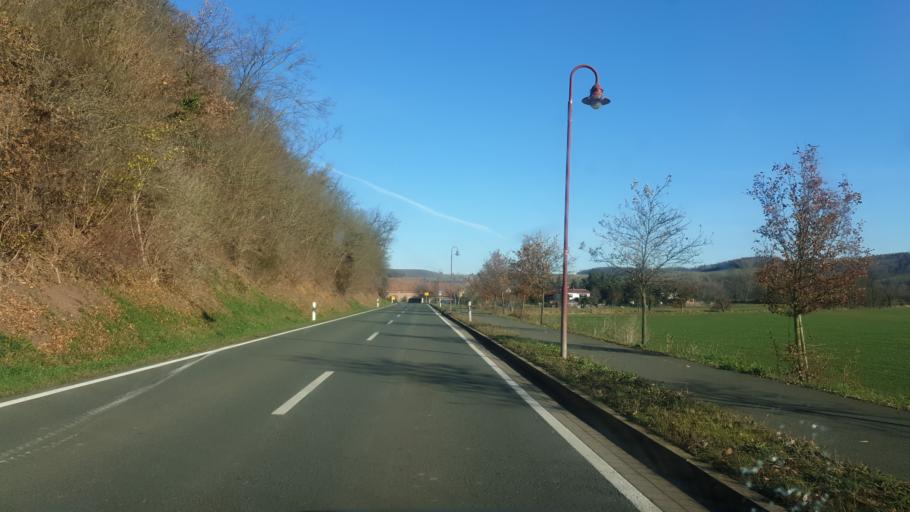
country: DE
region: Thuringia
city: Hartmannsdorf
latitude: 50.9823
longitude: 11.9831
